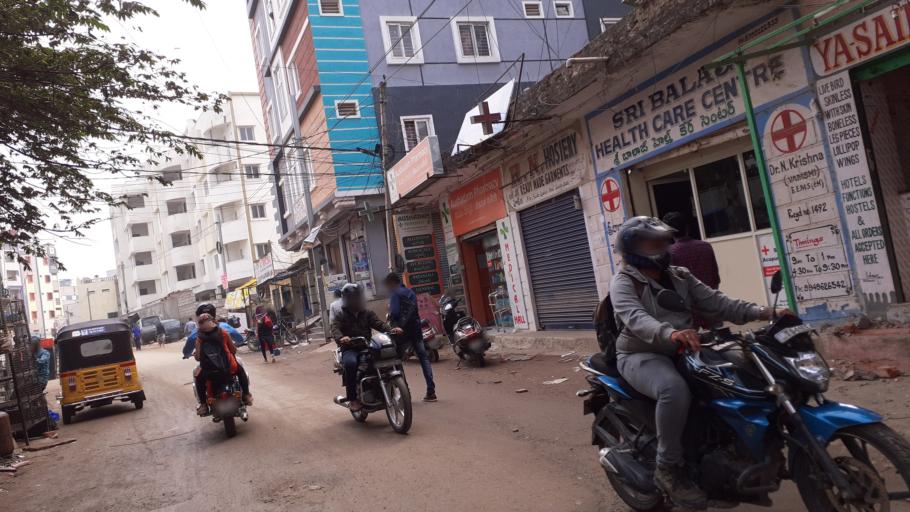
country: IN
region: Telangana
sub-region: Rangareddi
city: Kukatpalli
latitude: 17.4513
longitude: 78.3675
